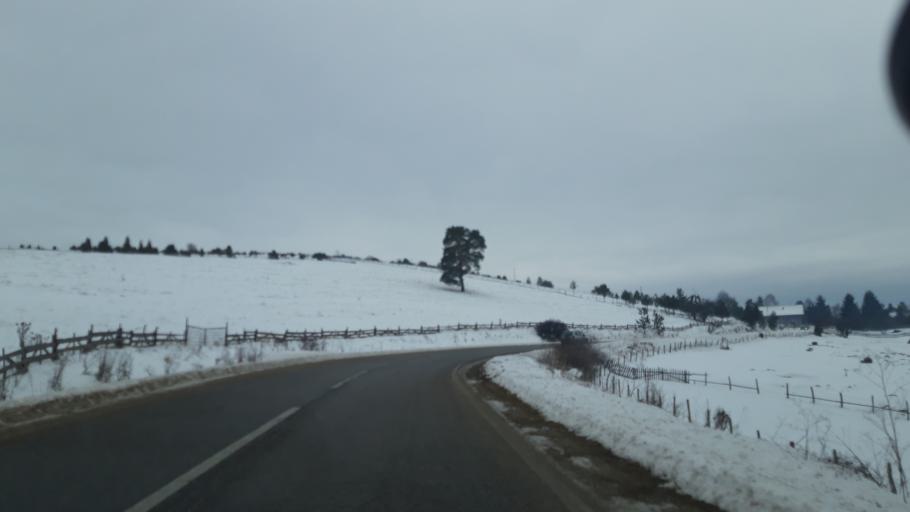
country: BA
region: Republika Srpska
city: Sokolac
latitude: 43.9518
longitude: 18.8424
